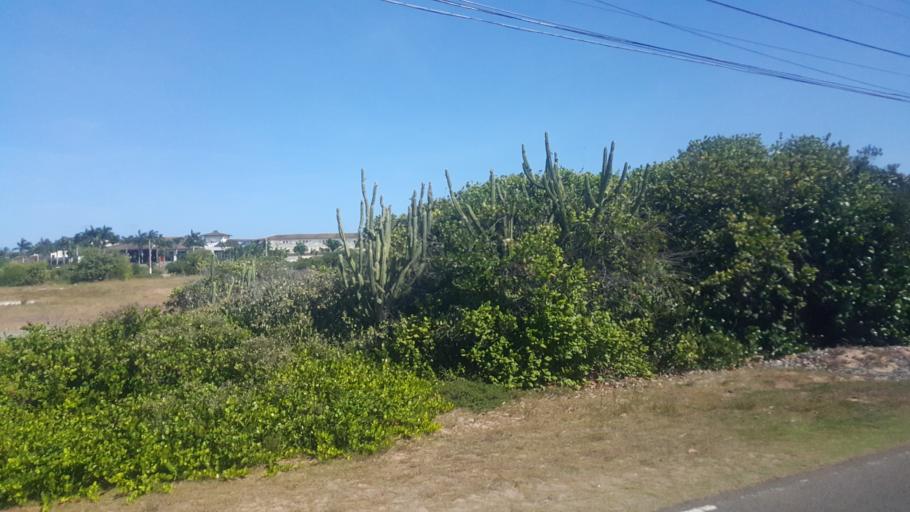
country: BR
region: Bahia
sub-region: Mata De Sao Joao
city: Mata de Sao Joao
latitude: -12.4373
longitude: -37.9222
